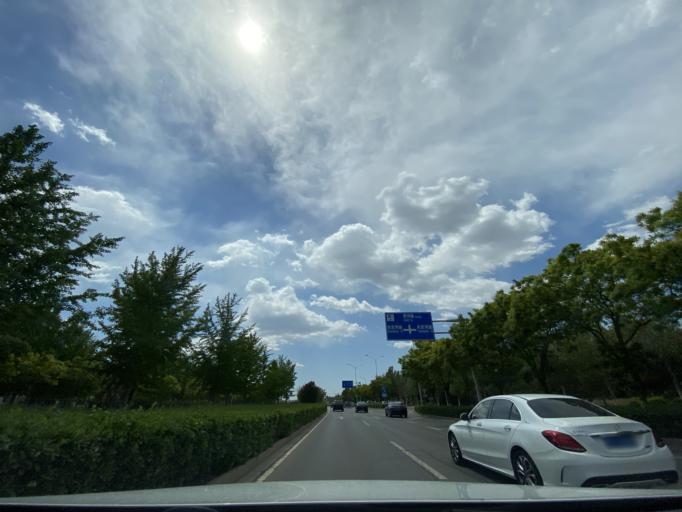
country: CN
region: Beijing
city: Sijiqing
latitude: 39.9409
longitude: 116.2403
